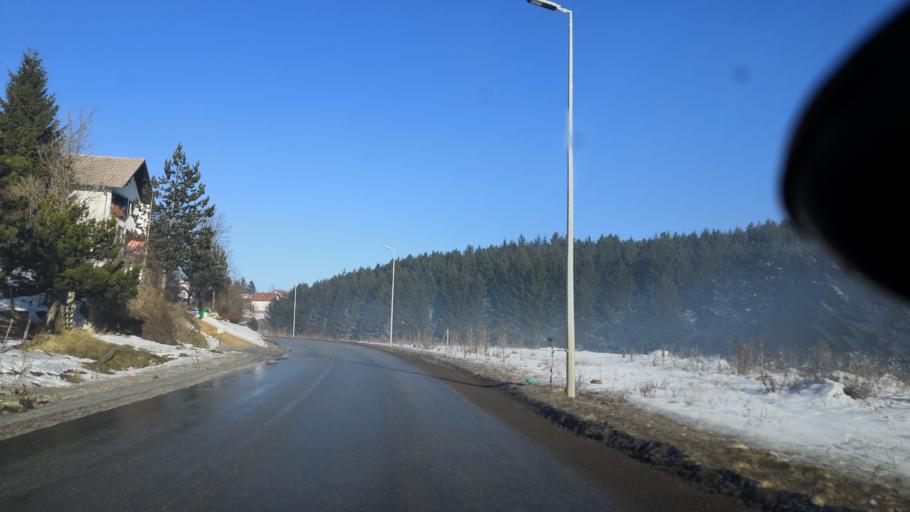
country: BA
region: Republika Srpska
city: Sokolac
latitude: 43.9351
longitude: 18.8042
